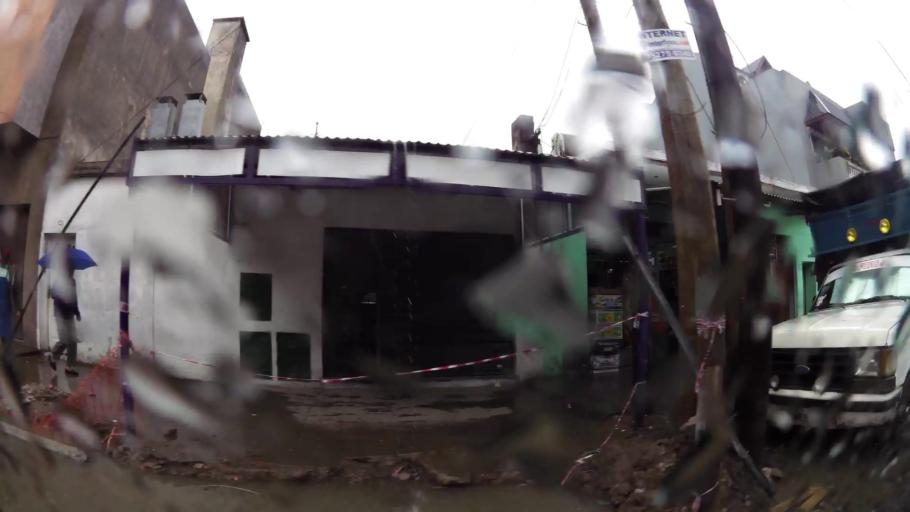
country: AR
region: Buenos Aires
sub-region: Partido de Lanus
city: Lanus
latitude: -34.7093
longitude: -58.4194
